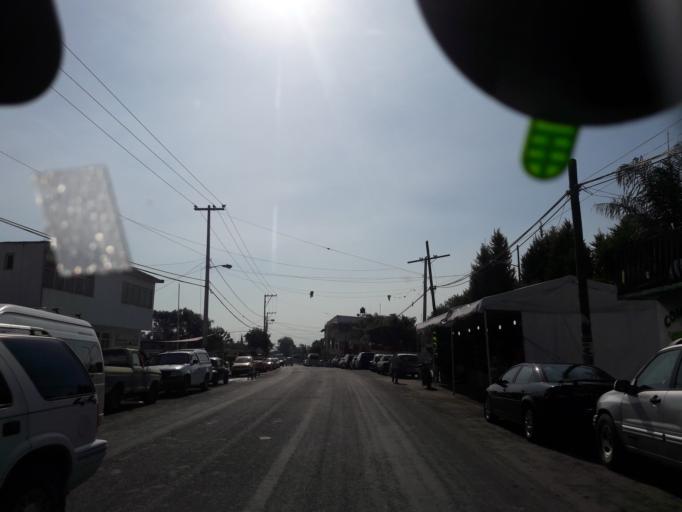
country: MX
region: Tlaxcala
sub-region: Ixtacuixtla de Mariano Matamoros
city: Villa Mariano Matamoros
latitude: 19.3083
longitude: -98.3757
